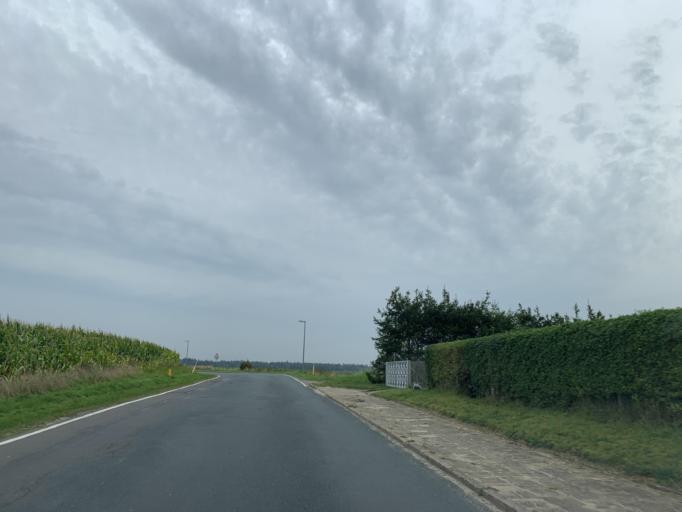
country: DE
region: Mecklenburg-Vorpommern
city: Woldegk
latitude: 53.3333
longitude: 13.6301
